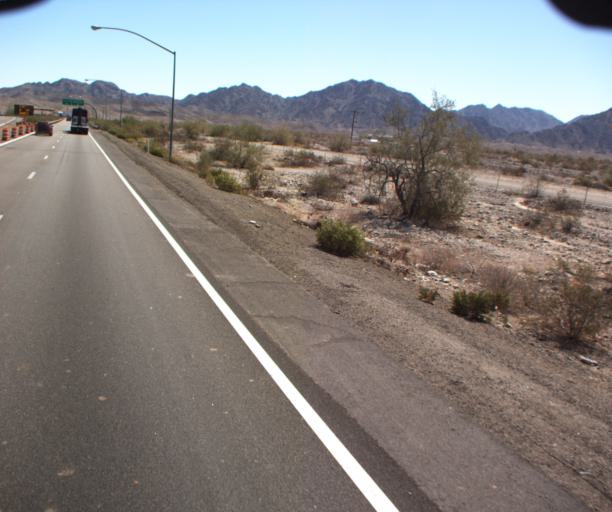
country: US
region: Arizona
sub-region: Yuma County
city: Fortuna Foothills
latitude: 32.6603
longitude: -114.3703
